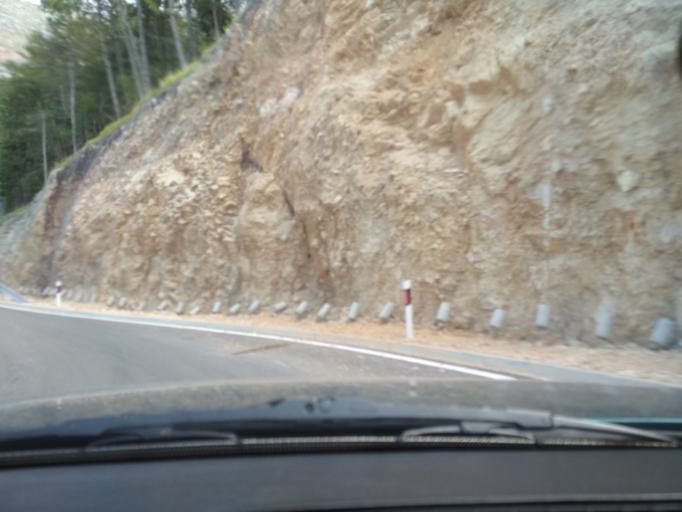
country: ME
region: Kotor
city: Kotor
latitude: 42.4352
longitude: 18.8408
